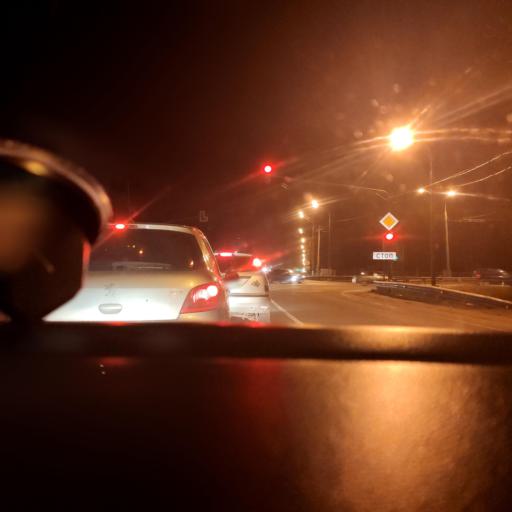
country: RU
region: Moskovskaya
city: Beloozerskiy
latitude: 55.3690
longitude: 38.3930
